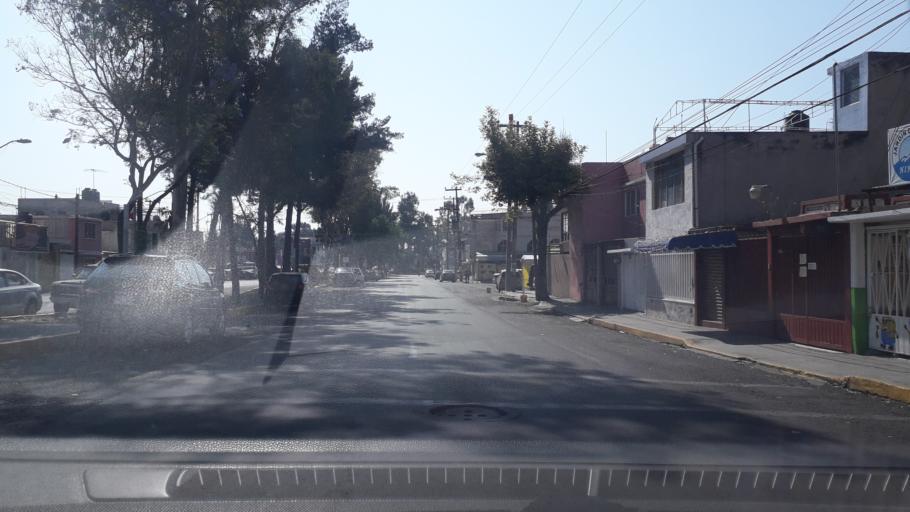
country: MX
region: Mexico City
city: Gustavo A. Madero
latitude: 19.5087
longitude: -99.0996
